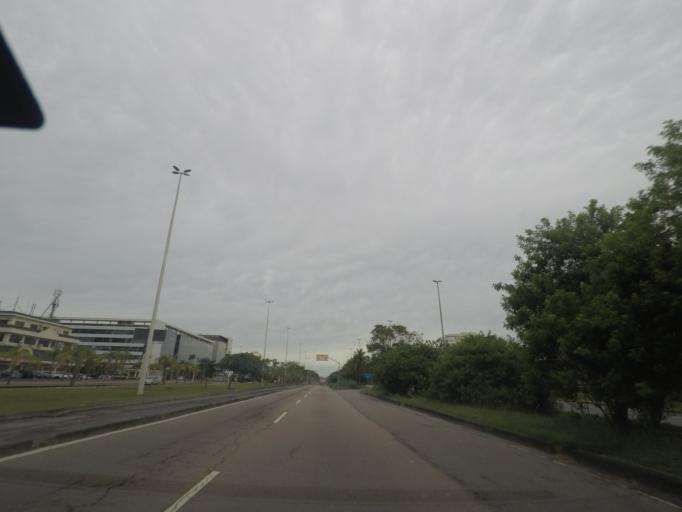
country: BR
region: Rio de Janeiro
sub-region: Nilopolis
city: Nilopolis
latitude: -23.0002
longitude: -43.3941
